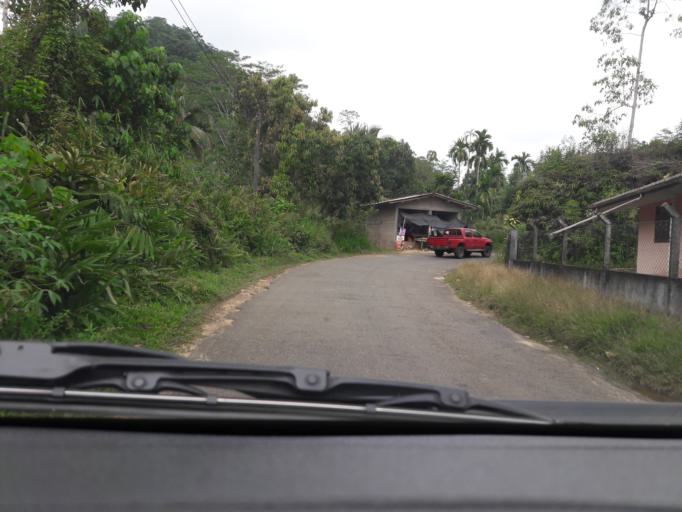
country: LK
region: Southern
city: Galle
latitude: 6.1842
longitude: 80.3045
